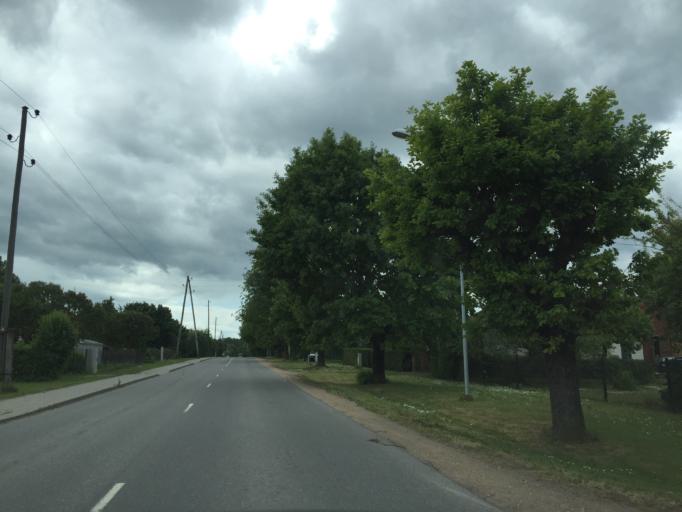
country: LV
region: Lecava
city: Iecava
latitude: 56.5988
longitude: 24.2175
